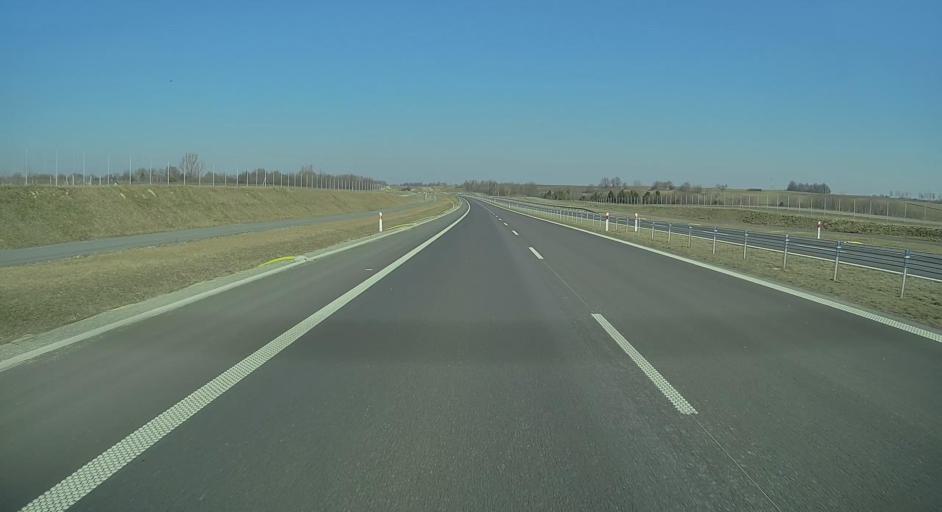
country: PL
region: Lublin Voivodeship
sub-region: Powiat janowski
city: Modliborzyce
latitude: 50.8044
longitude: 22.2980
